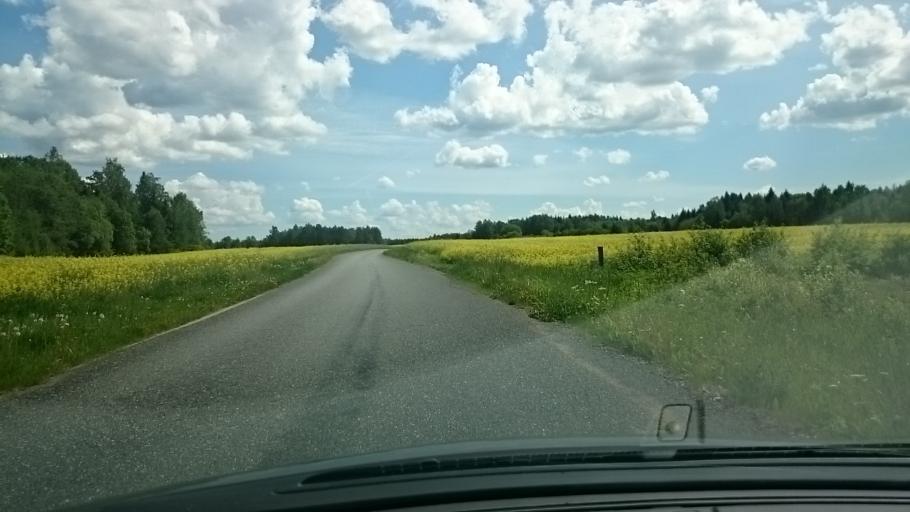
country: EE
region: Harju
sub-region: Anija vald
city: Kehra
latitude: 59.1037
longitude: 25.3148
